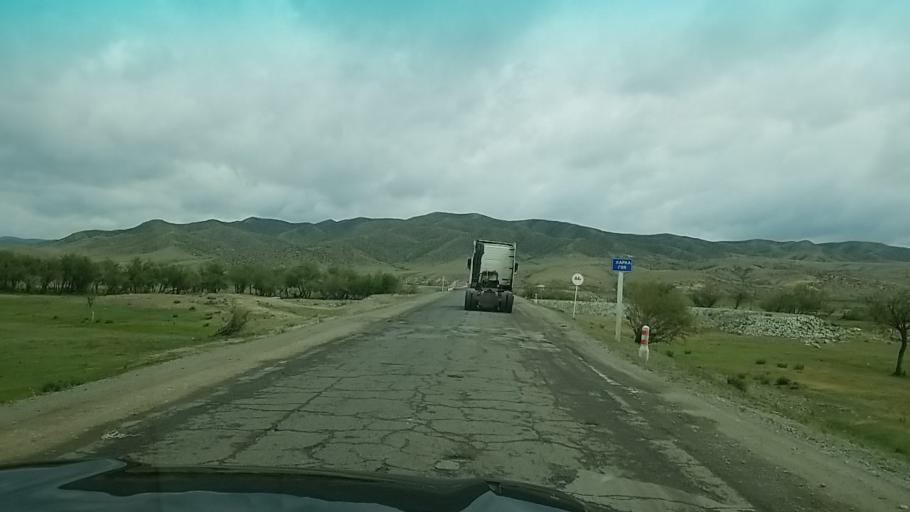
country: MN
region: Central Aimak
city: Javhlant
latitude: 48.8866
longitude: 106.0963
